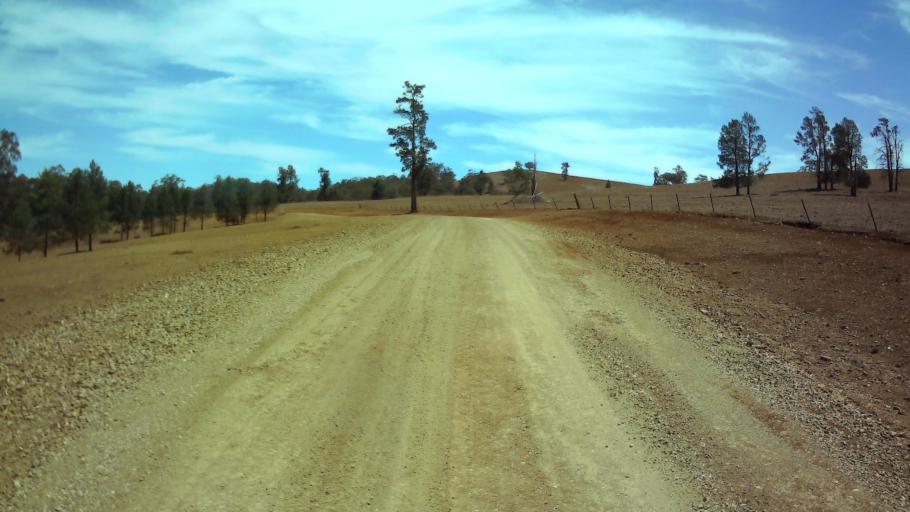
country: AU
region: New South Wales
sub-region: Weddin
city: Grenfell
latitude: -33.7950
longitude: 148.1601
